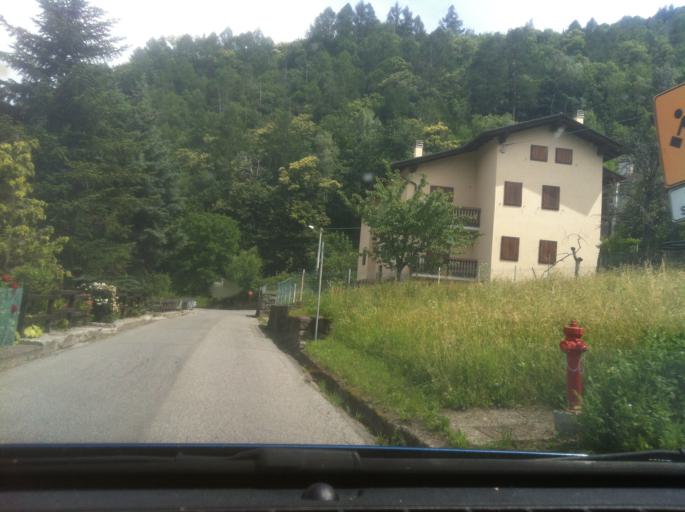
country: IT
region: Aosta Valley
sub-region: Valle d'Aosta
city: Saint Marcel
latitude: 45.7282
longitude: 7.4469
